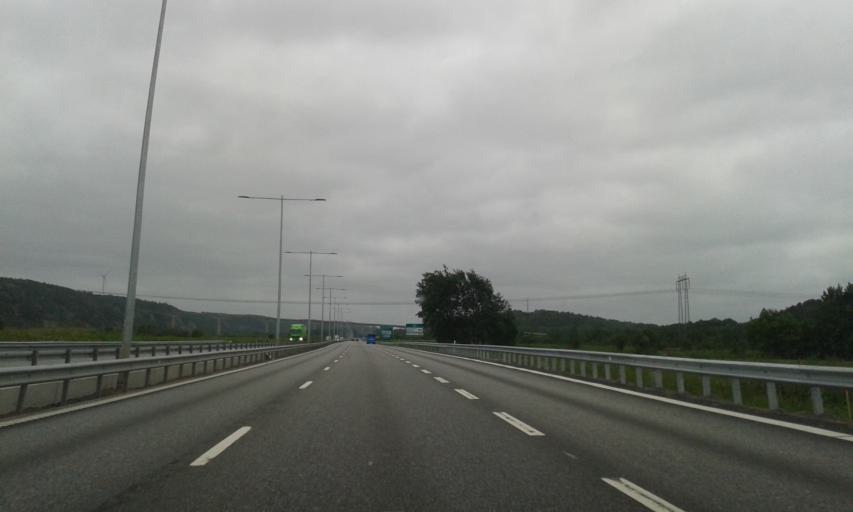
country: SE
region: Vaestra Goetaland
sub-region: Ale Kommun
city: Surte
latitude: 57.8203
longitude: 12.0042
